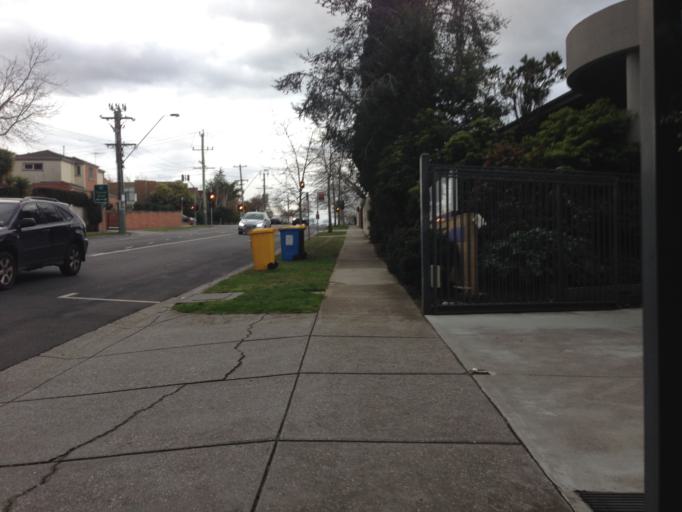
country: AU
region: Victoria
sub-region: Boroondara
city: Camberwell
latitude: -37.8481
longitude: 145.0685
